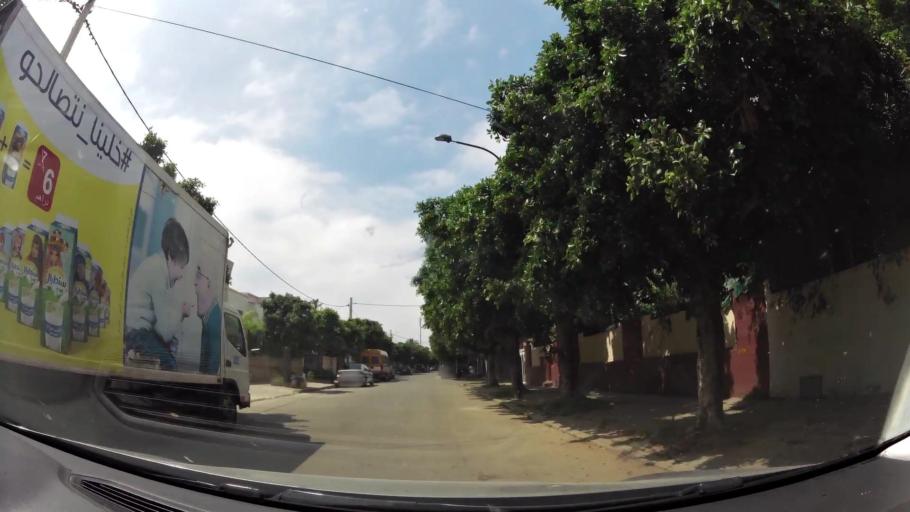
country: MA
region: Rabat-Sale-Zemmour-Zaer
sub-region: Rabat
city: Rabat
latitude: 34.0129
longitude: -6.8444
